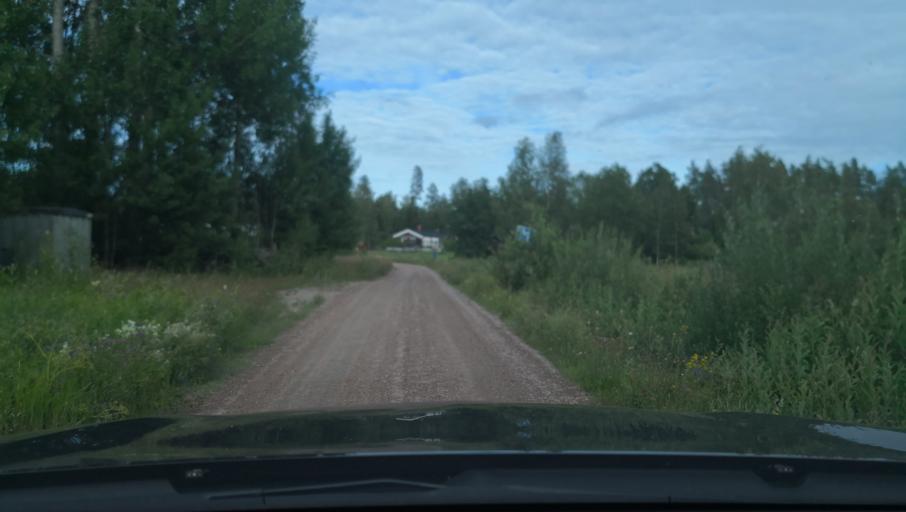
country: SE
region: Vaestmanland
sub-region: Surahammars Kommun
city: Surahammar
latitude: 59.6577
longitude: 16.1384
